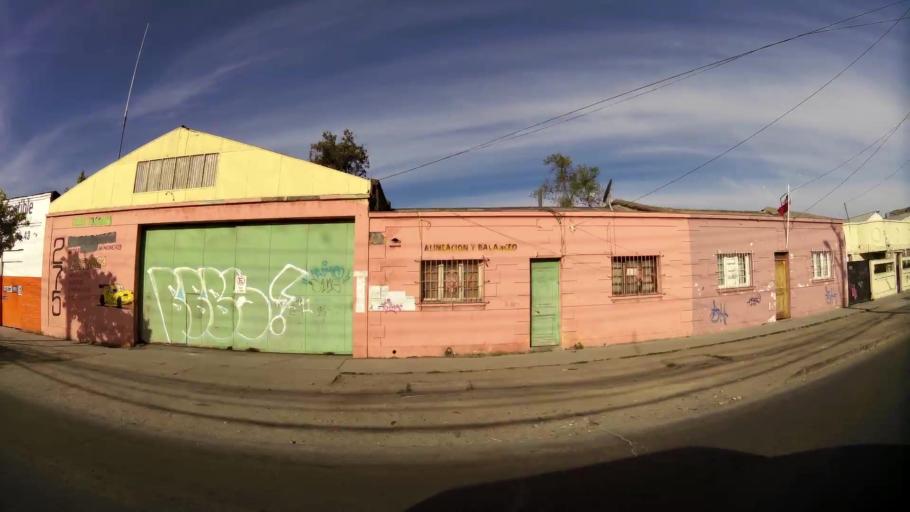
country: CL
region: Santiago Metropolitan
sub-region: Provincia de Cordillera
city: Puente Alto
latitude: -33.6089
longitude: -70.5704
